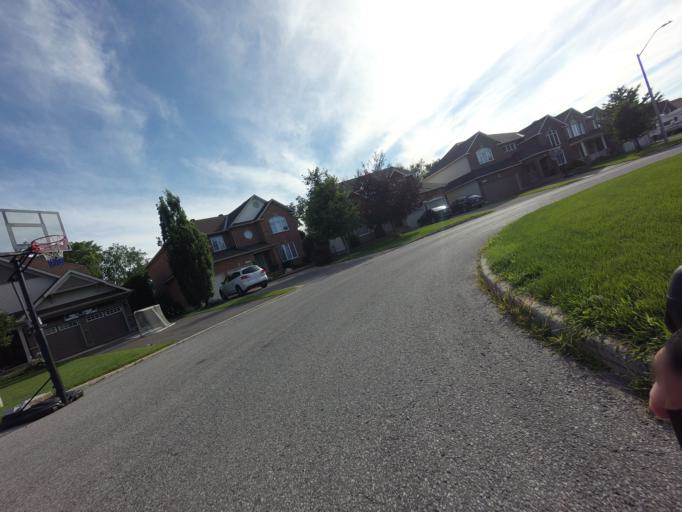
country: CA
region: Ontario
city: Ottawa
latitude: 45.2870
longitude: -75.6903
